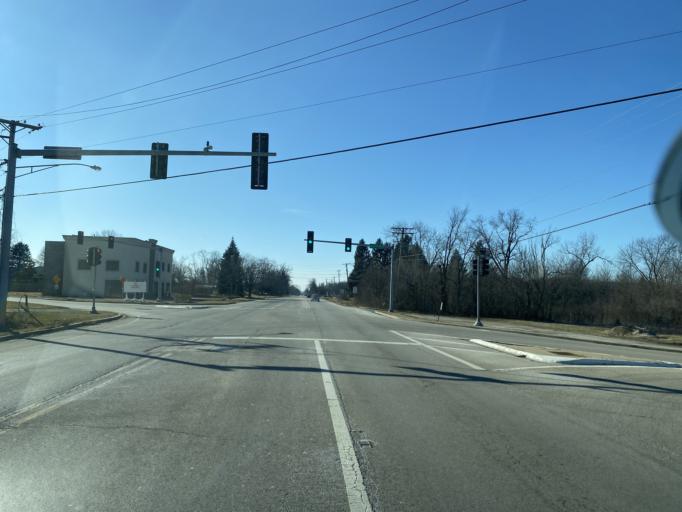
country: US
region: Illinois
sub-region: Will County
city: Lockport
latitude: 41.6231
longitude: -88.0269
